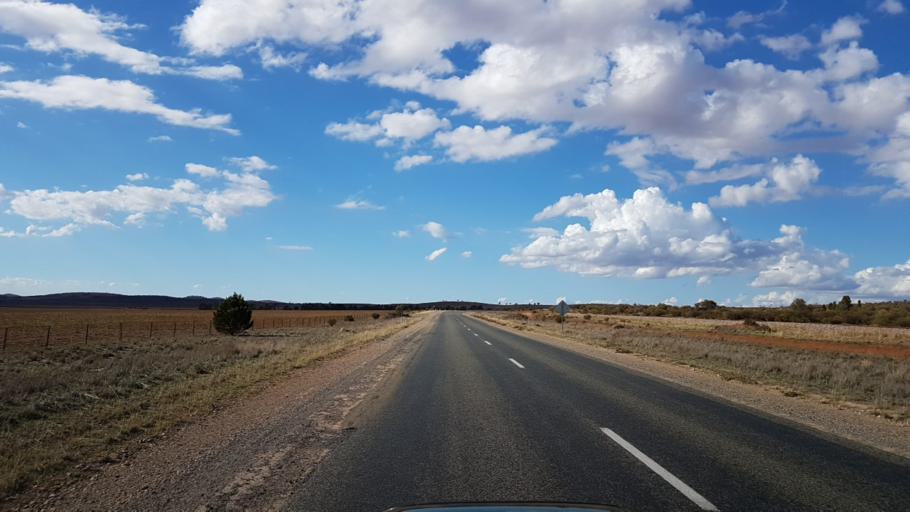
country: AU
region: South Australia
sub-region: Peterborough
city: Peterborough
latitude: -32.9587
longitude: 138.8933
